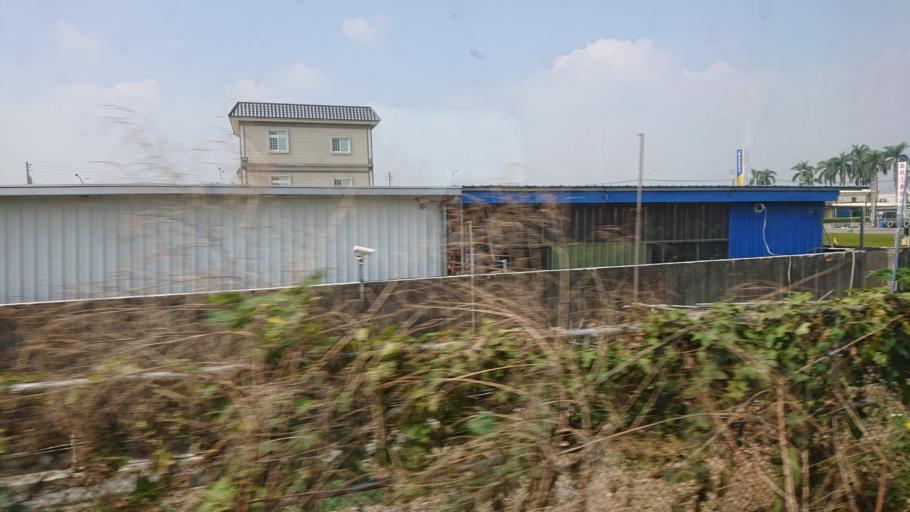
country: TW
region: Taiwan
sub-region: Yunlin
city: Douliu
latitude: 23.6505
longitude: 120.4728
